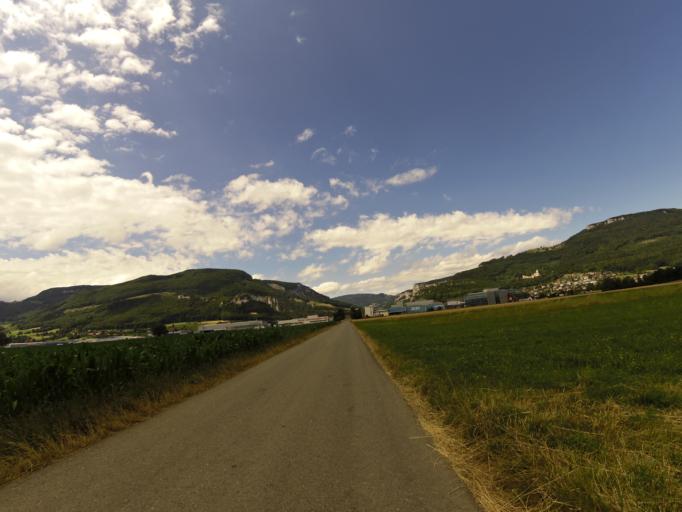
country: CH
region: Solothurn
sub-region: Bezirk Gaeu
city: Oensingen
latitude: 47.2778
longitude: 7.7238
